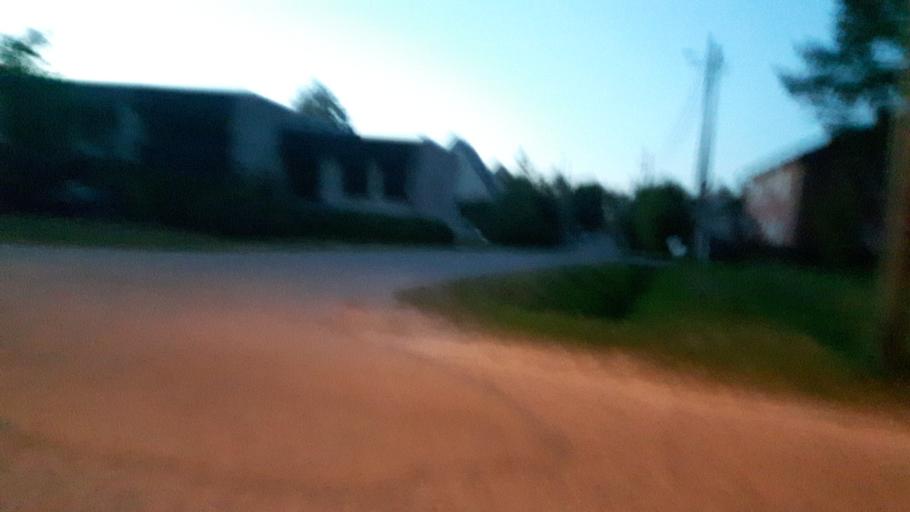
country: EE
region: Paernumaa
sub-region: Paernu linn
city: Parnu
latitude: 58.3574
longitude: 24.5557
